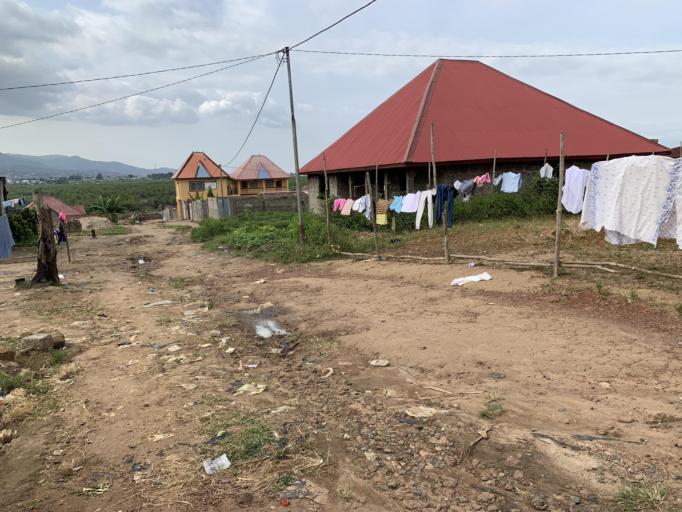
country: SL
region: Western Area
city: Hastings
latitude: 8.3974
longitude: -13.1181
